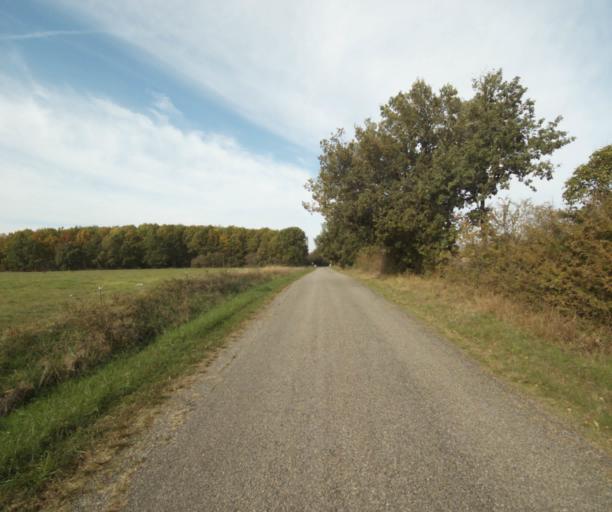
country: FR
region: Midi-Pyrenees
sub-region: Departement du Tarn-et-Garonne
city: Orgueil
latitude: 43.9020
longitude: 1.4095
